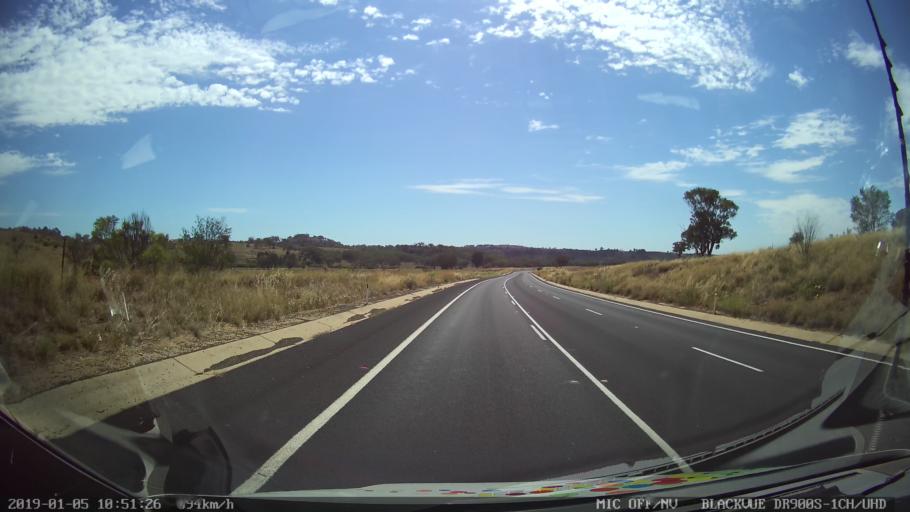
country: AU
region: New South Wales
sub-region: Warrumbungle Shire
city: Coonabarabran
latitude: -31.4251
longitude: 149.0896
